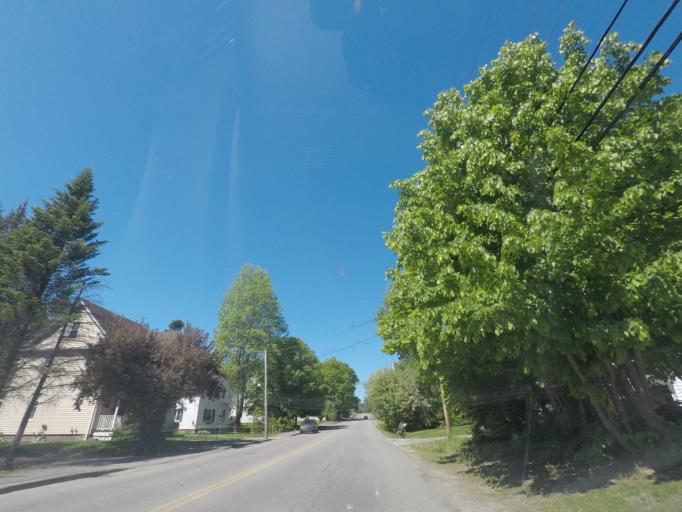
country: US
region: Maine
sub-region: Kennebec County
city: Gardiner
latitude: 44.2326
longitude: -69.7848
